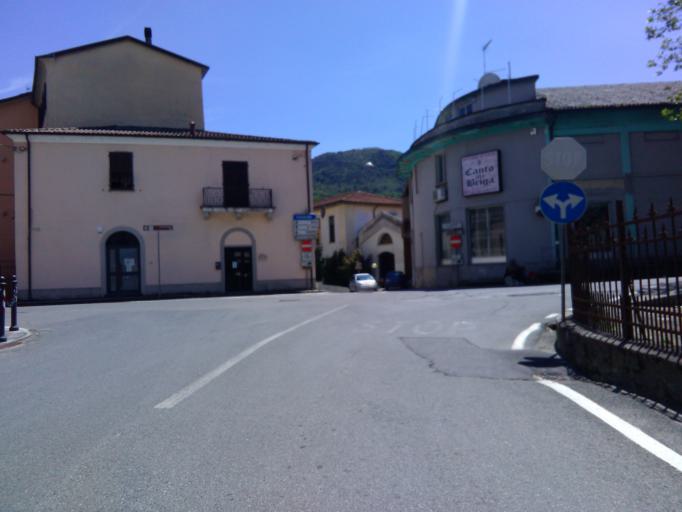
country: IT
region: Tuscany
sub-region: Provincia di Massa-Carrara
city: Aulla
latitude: 44.2075
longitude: 9.9677
